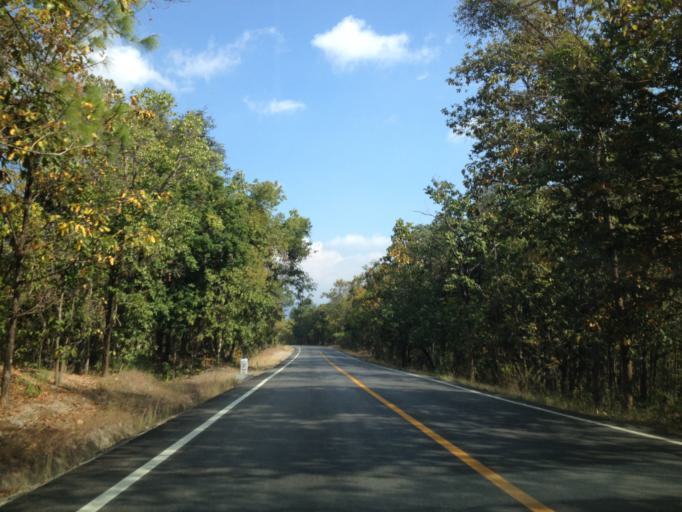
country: TH
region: Chiang Mai
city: Hot
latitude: 18.1556
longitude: 98.4300
